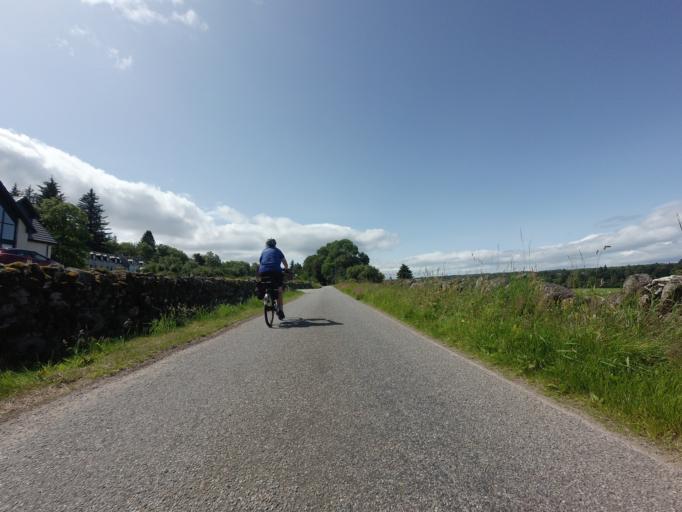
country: GB
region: Scotland
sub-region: Highland
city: Nairn
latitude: 57.5031
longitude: -3.9965
